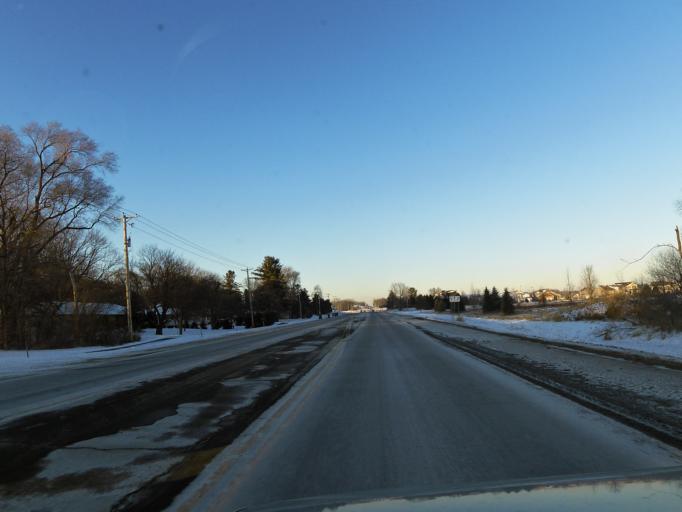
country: US
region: Minnesota
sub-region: Dakota County
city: Farmington
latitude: 44.6665
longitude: -93.1366
